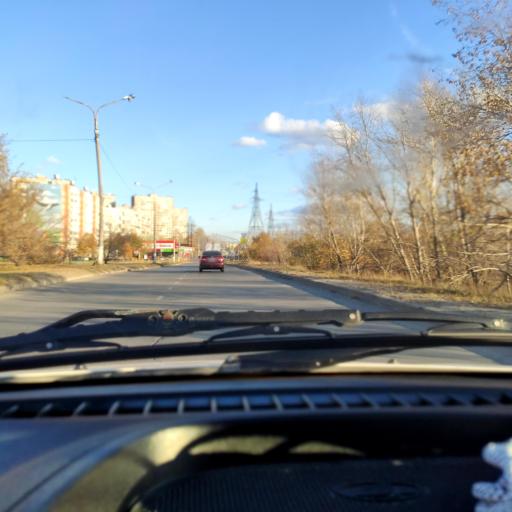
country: RU
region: Samara
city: Zhigulevsk
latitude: 53.4817
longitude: 49.5161
